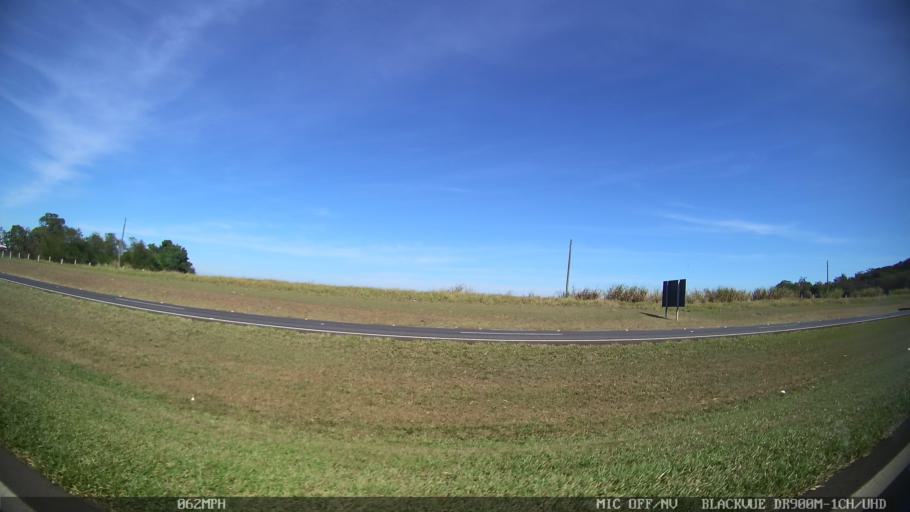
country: BR
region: Sao Paulo
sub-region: Santa Rita Do Passa Quatro
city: Santa Rita do Passa Quatro
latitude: -21.7776
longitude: -47.5362
